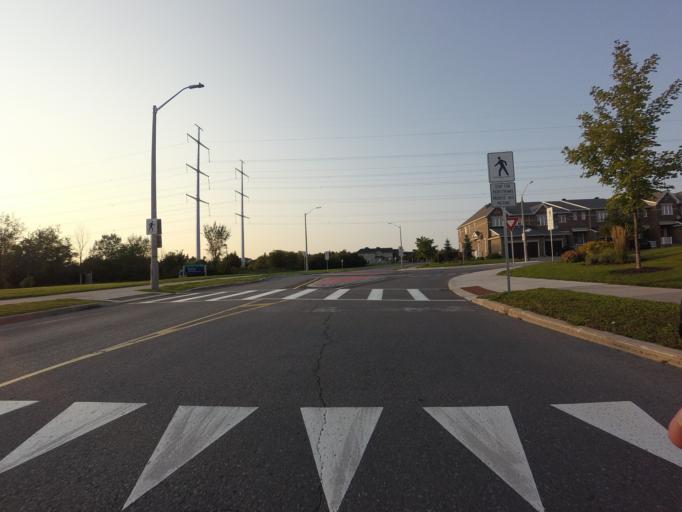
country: CA
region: Ontario
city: Bells Corners
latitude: 45.2859
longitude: -75.8577
